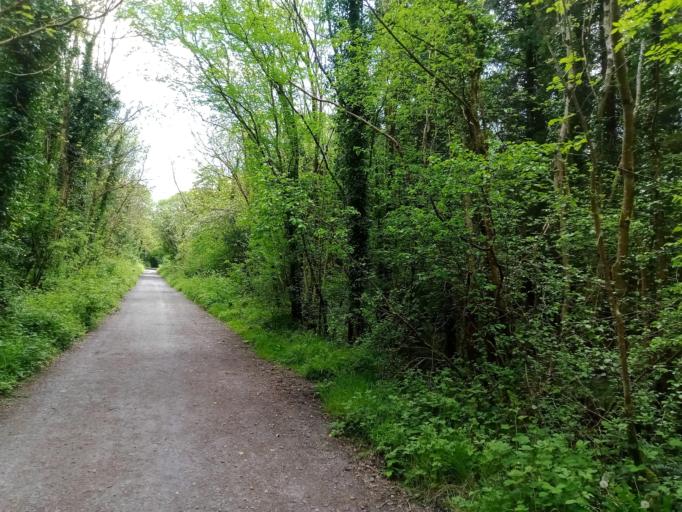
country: IE
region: Leinster
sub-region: Kilkenny
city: Castlecomer
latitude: 52.8158
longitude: -7.2009
